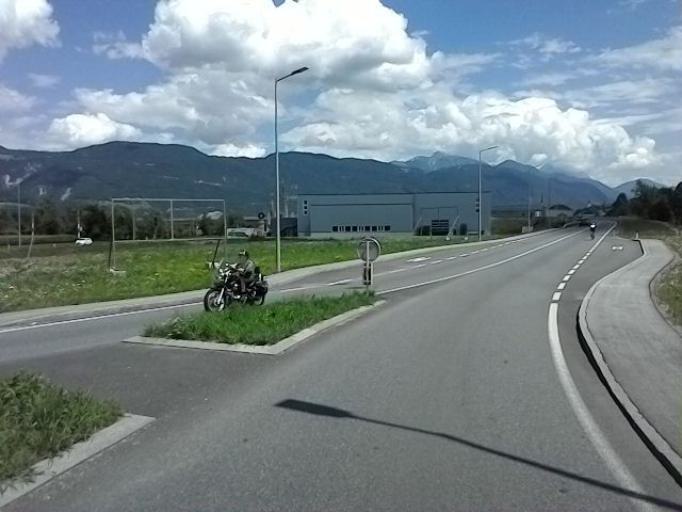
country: AT
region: Tyrol
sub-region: Politischer Bezirk Innsbruck Land
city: Telfs
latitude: 47.2986
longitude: 11.0657
